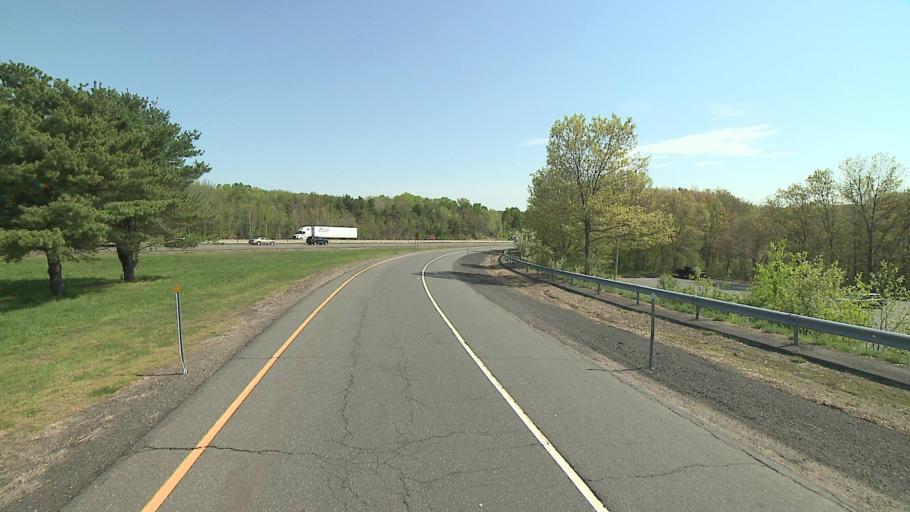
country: US
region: Connecticut
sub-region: Tolland County
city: Tolland
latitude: 41.8862
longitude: -72.3102
